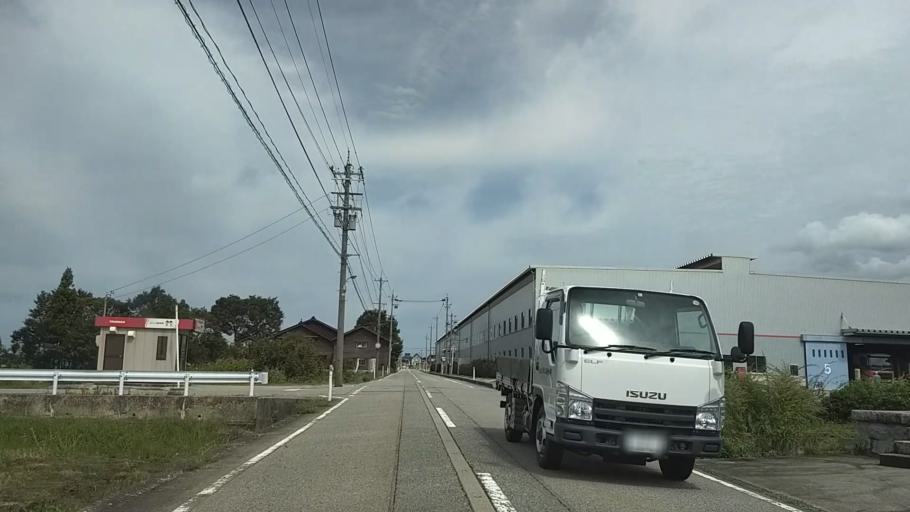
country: JP
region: Toyama
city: Kamiichi
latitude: 36.7434
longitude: 137.3735
